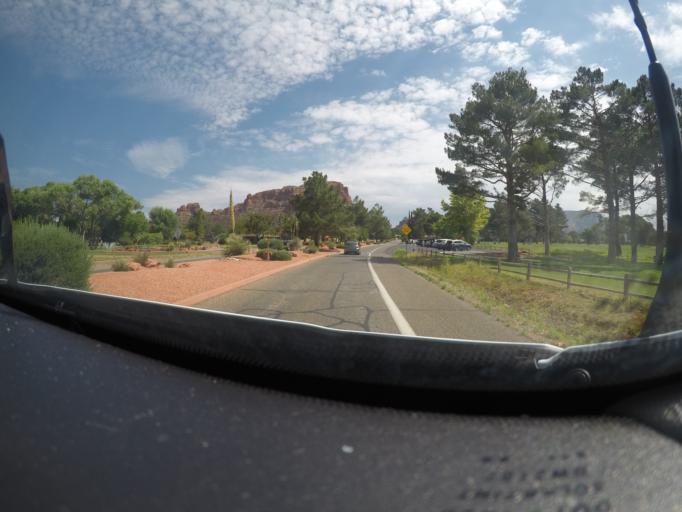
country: US
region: Arizona
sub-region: Yavapai County
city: Big Park
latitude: 34.7804
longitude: -111.7749
